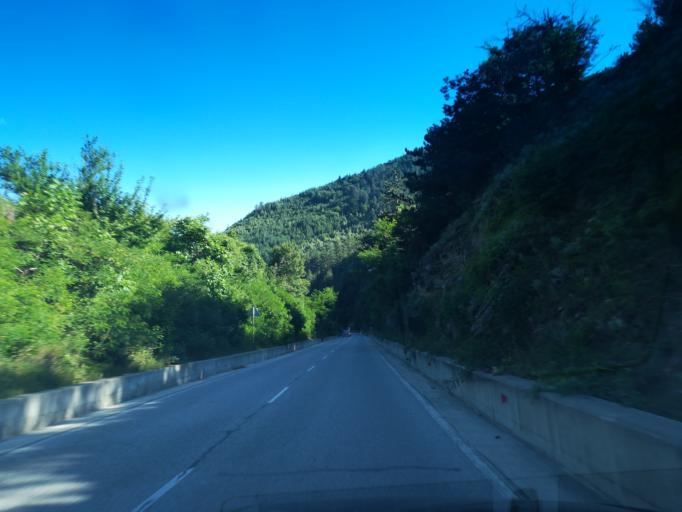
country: BG
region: Smolyan
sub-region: Obshtina Chepelare
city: Chepelare
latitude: 41.8386
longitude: 24.6796
